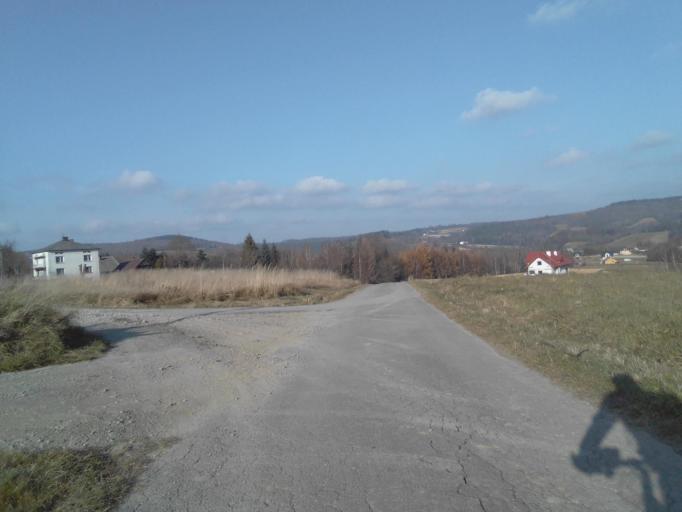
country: PL
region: Subcarpathian Voivodeship
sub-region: Powiat strzyzowski
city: Gwoznica Gorna
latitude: 49.8323
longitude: 21.9747
